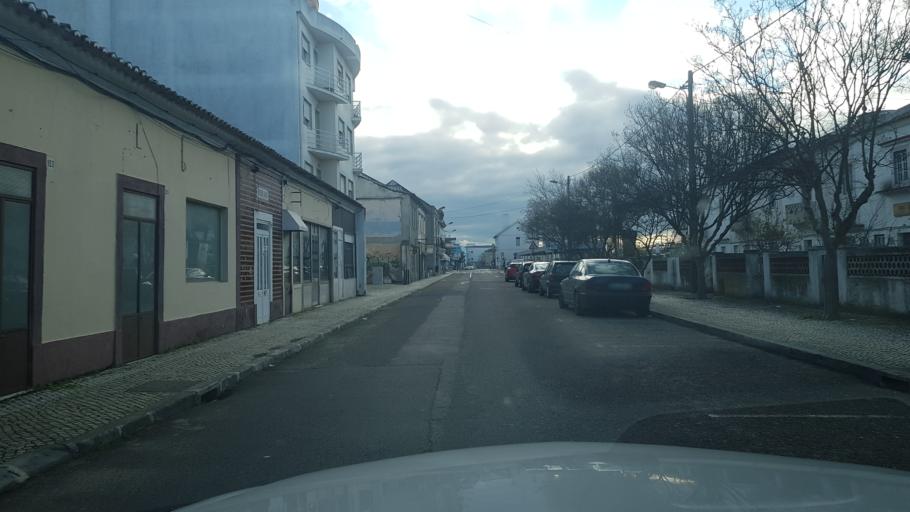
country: PT
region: Santarem
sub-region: Entroncamento
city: Entroncamento
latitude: 39.4623
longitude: -8.4719
